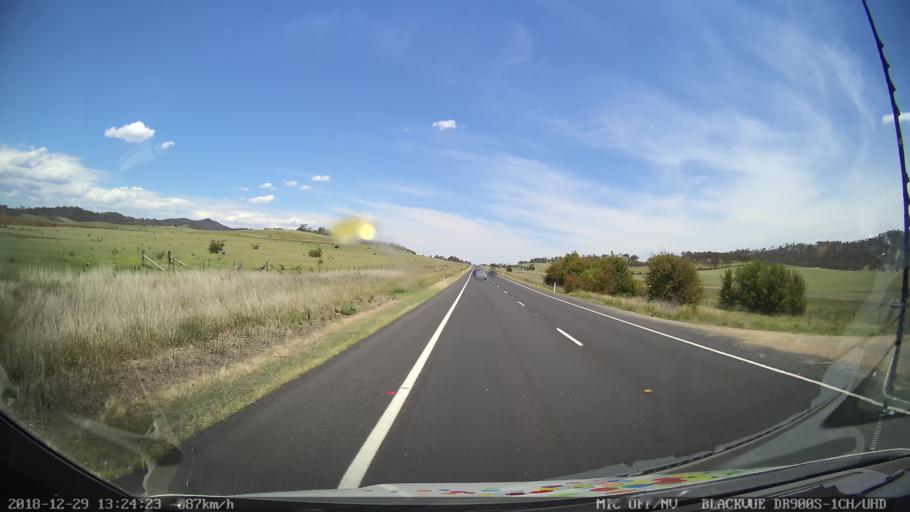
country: AU
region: New South Wales
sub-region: Cooma-Monaro
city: Cooma
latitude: -35.8289
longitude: 149.1625
